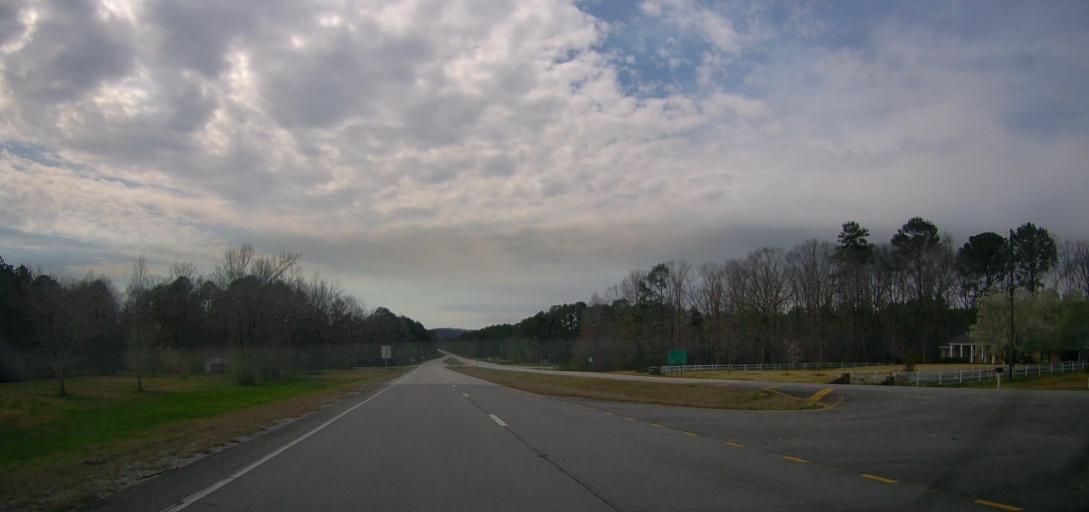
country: US
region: Alabama
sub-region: Marion County
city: Winfield
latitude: 33.9327
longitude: -87.7041
